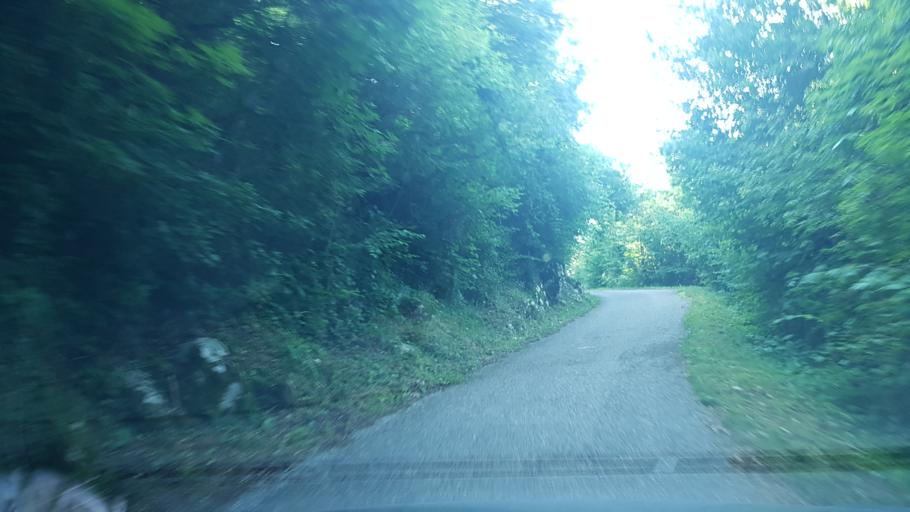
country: IT
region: Friuli Venezia Giulia
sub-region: Provincia di Udine
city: Nimis
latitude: 46.2321
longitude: 13.2519
